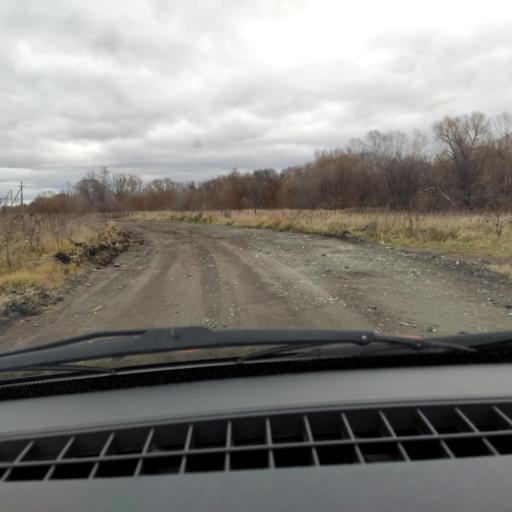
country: RU
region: Bashkortostan
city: Avdon
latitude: 54.4955
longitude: 55.8624
